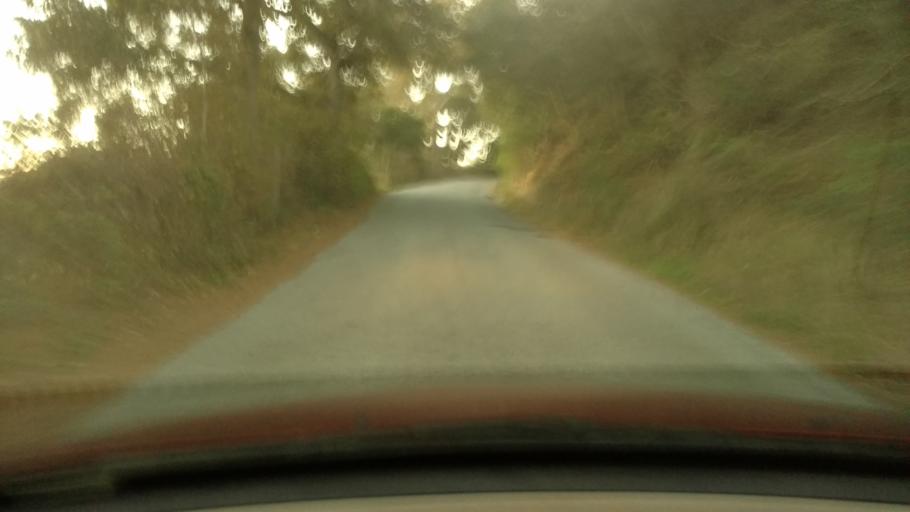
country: US
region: California
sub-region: Santa Cruz County
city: Interlaken
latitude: 36.9970
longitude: -121.7342
